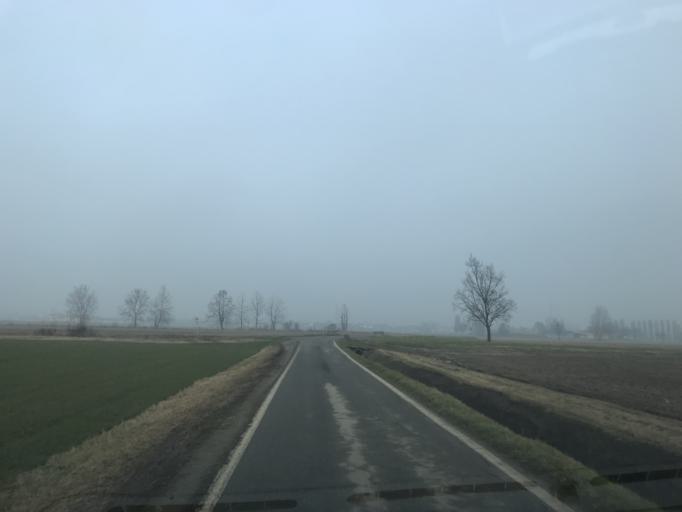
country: IT
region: Lombardy
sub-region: Provincia di Lodi
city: Ossago Lodigiano
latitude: 45.2373
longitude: 9.5263
